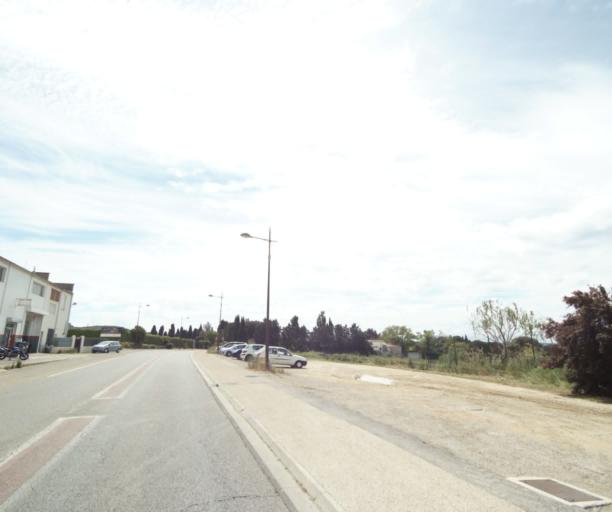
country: FR
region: Provence-Alpes-Cote d'Azur
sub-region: Departement des Bouches-du-Rhone
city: Rognac
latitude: 43.4958
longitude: 5.2298
